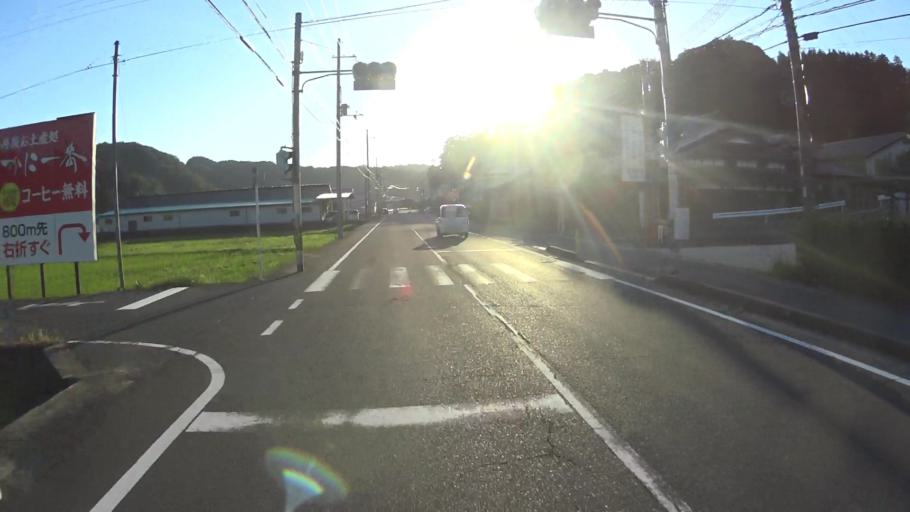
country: JP
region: Hyogo
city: Toyooka
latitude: 35.6525
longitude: 134.9795
